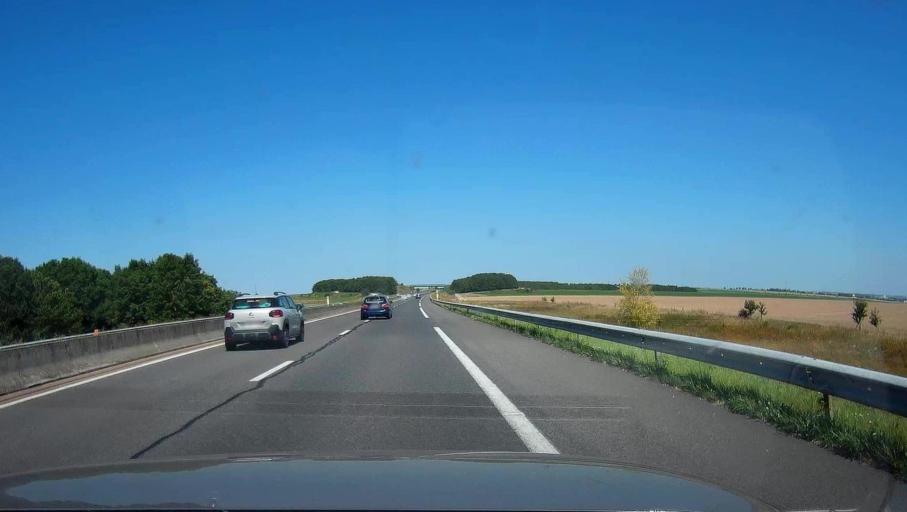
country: FR
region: Champagne-Ardenne
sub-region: Departement de la Marne
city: Fagnieres
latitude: 48.9322
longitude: 4.2846
